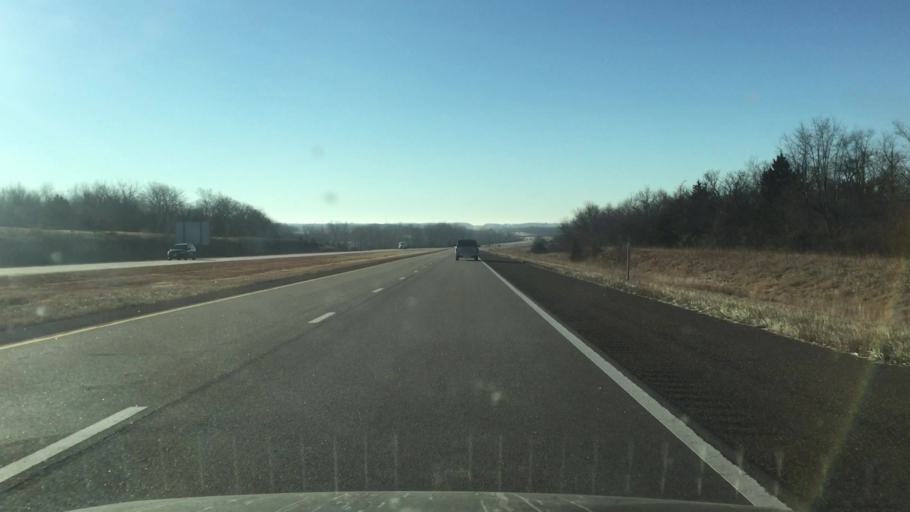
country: US
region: Kansas
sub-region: Johnson County
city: Spring Hill
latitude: 38.7116
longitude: -94.8347
